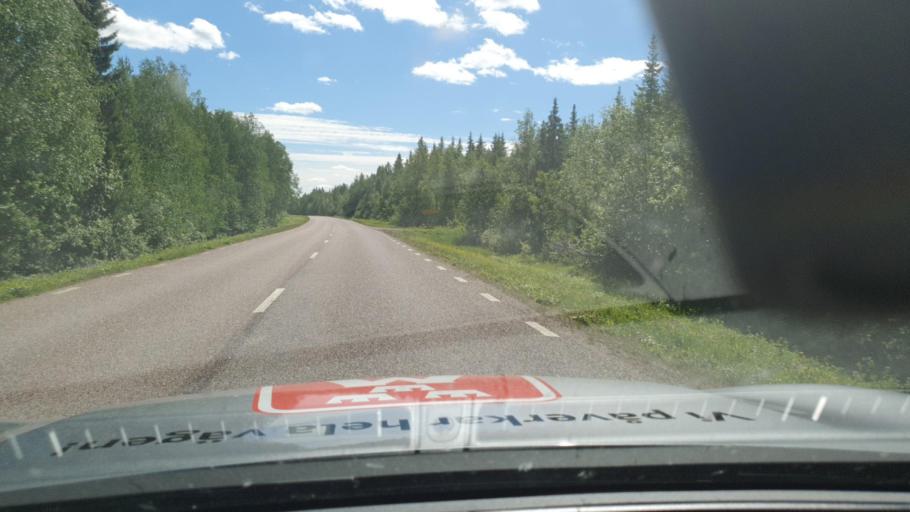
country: FI
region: Lapland
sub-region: Tunturi-Lappi
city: Kolari
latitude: 67.0736
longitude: 23.6608
